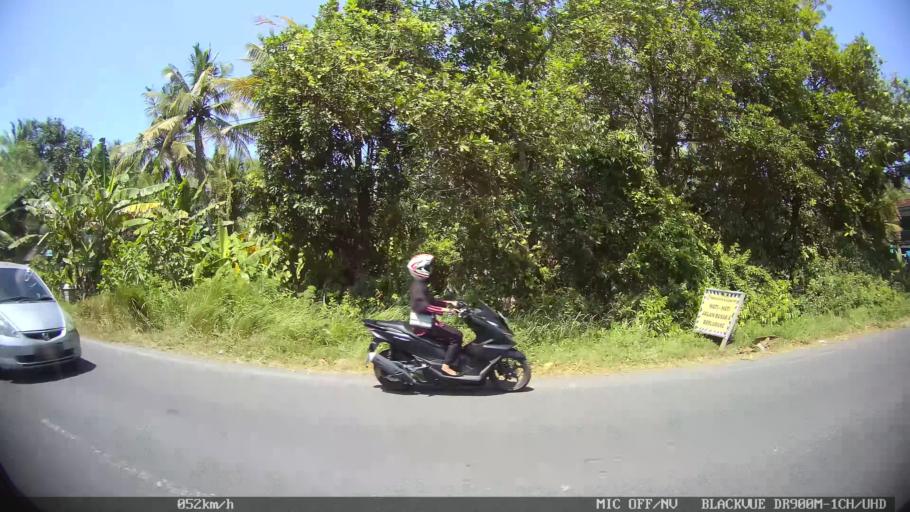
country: ID
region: Daerah Istimewa Yogyakarta
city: Srandakan
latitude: -7.9335
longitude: 110.1444
